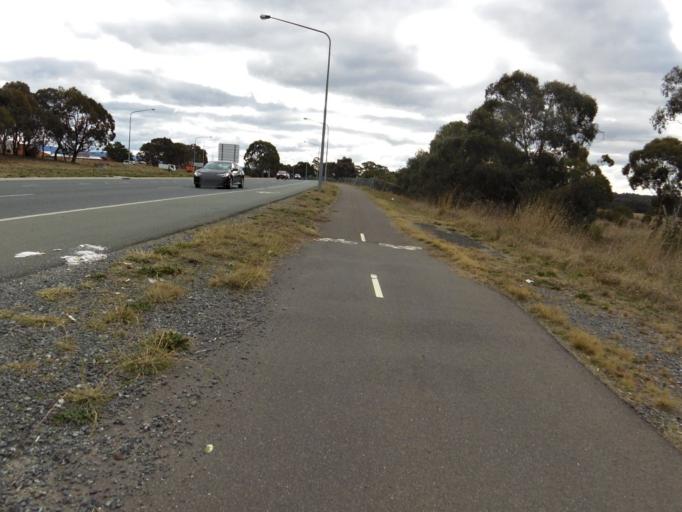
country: AU
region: Australian Capital Territory
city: Belconnen
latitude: -35.2324
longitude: 149.0856
